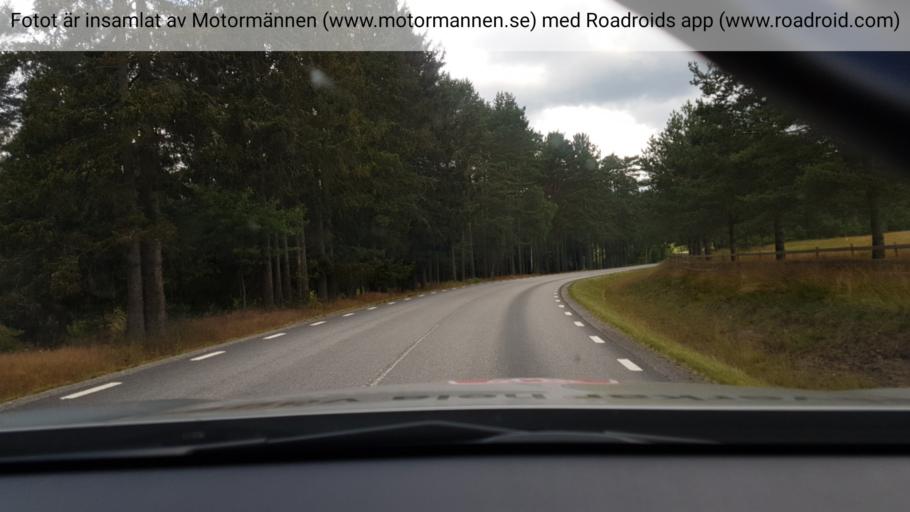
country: SE
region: Vaestra Goetaland
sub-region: Svenljunga Kommun
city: Svenljunga
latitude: 57.4649
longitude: 13.1725
